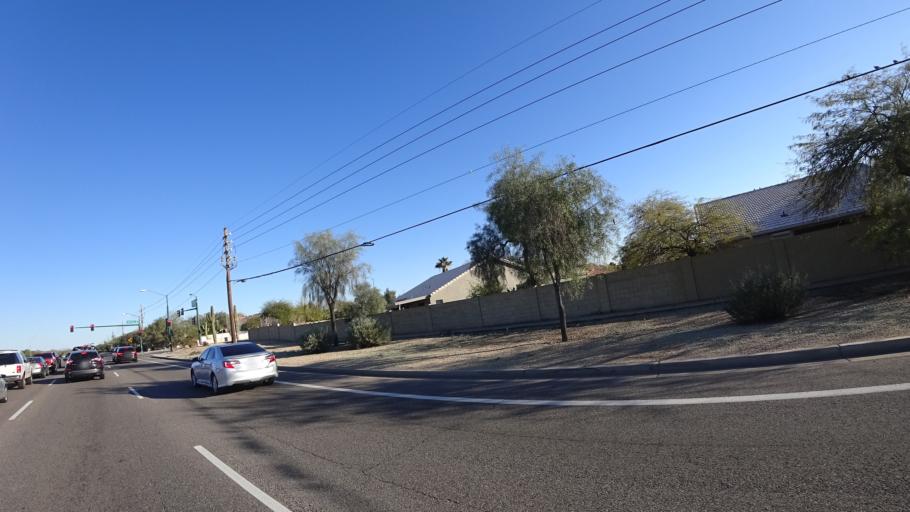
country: US
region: Arizona
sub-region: Maricopa County
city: Peoria
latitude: 33.7124
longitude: -112.1796
